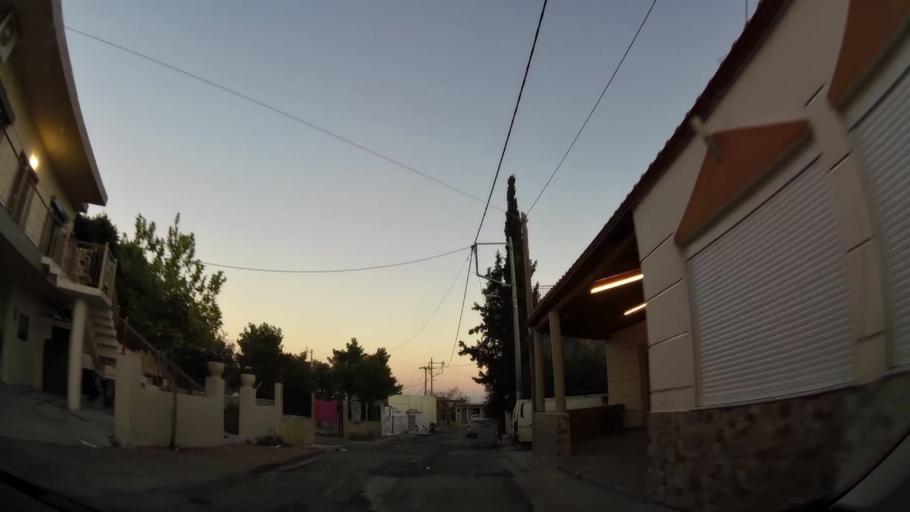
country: GR
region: Attica
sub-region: Nomarchia Dytikis Attikis
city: Ano Liosia
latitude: 38.0808
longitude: 23.6958
